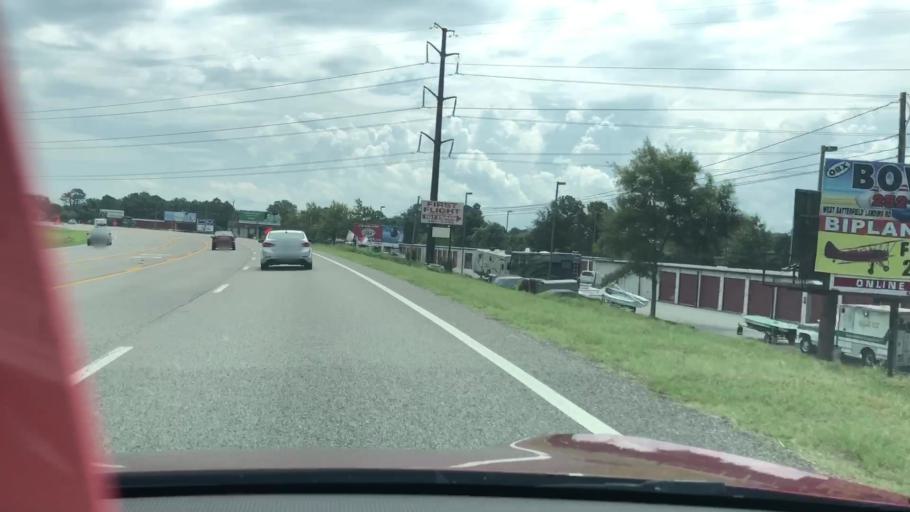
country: US
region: North Carolina
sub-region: Dare County
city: Southern Shores
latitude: 36.0843
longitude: -75.7967
